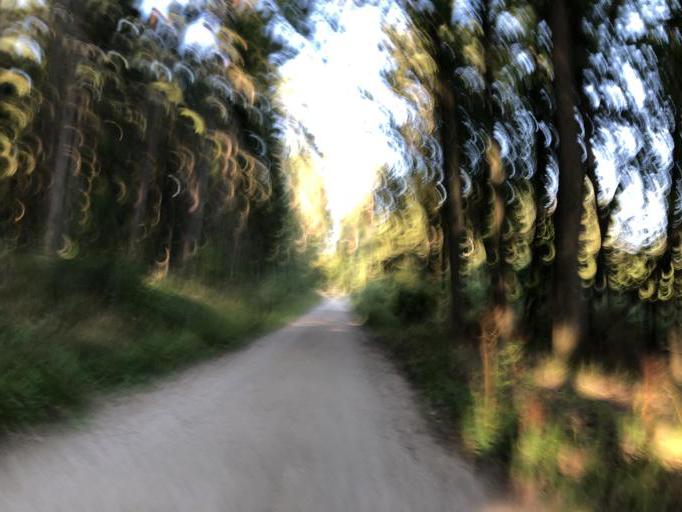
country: DE
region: Bavaria
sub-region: Regierungsbezirk Mittelfranken
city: Kalchreuth
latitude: 49.5449
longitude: 11.0966
